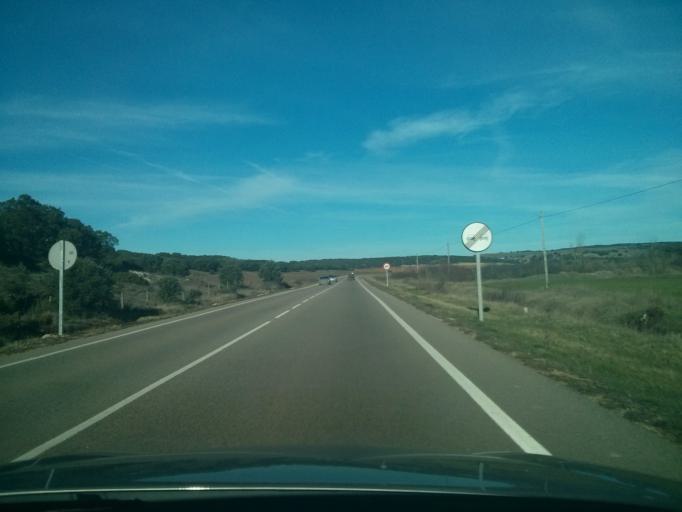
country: ES
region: Castille and Leon
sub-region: Provincia de Burgos
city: Abajas
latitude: 42.6120
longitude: -3.6331
